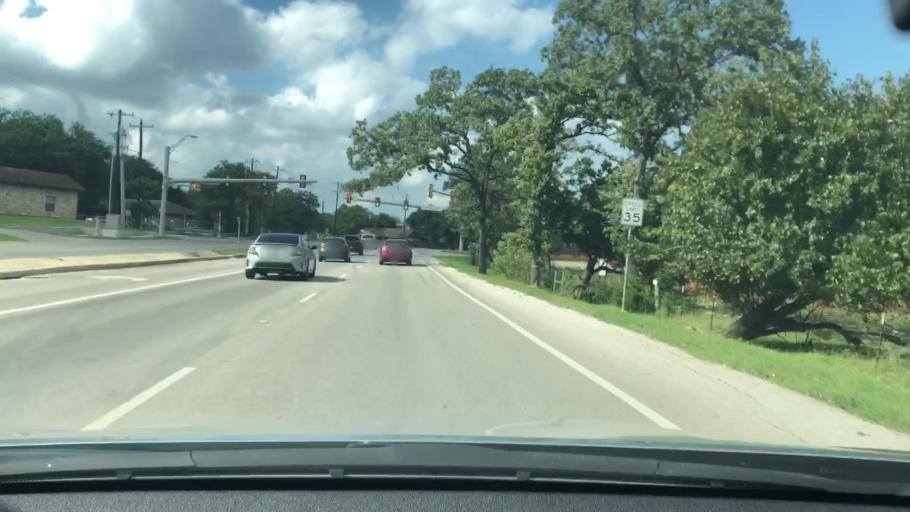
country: US
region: Texas
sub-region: Kendall County
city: Boerne
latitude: 29.7827
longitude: -98.7168
